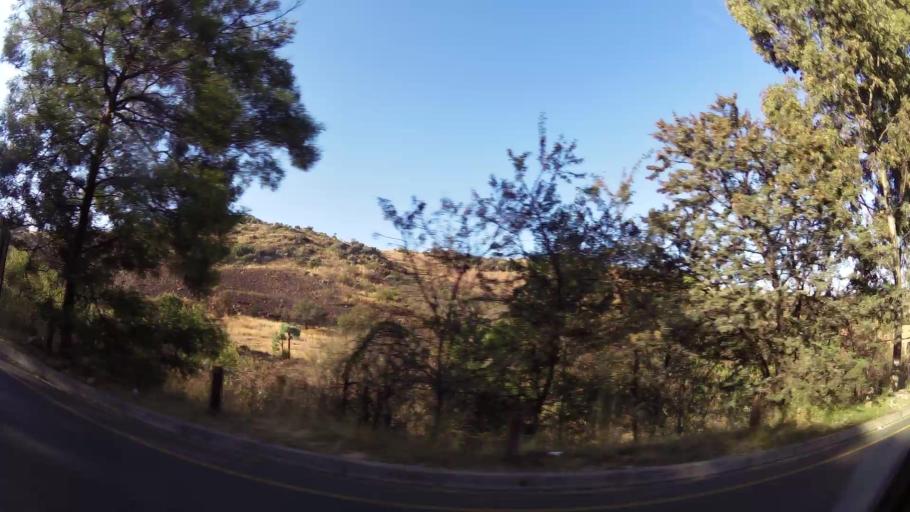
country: ZA
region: Gauteng
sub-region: City of Johannesburg Metropolitan Municipality
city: Johannesburg
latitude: -26.2745
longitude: 28.0637
